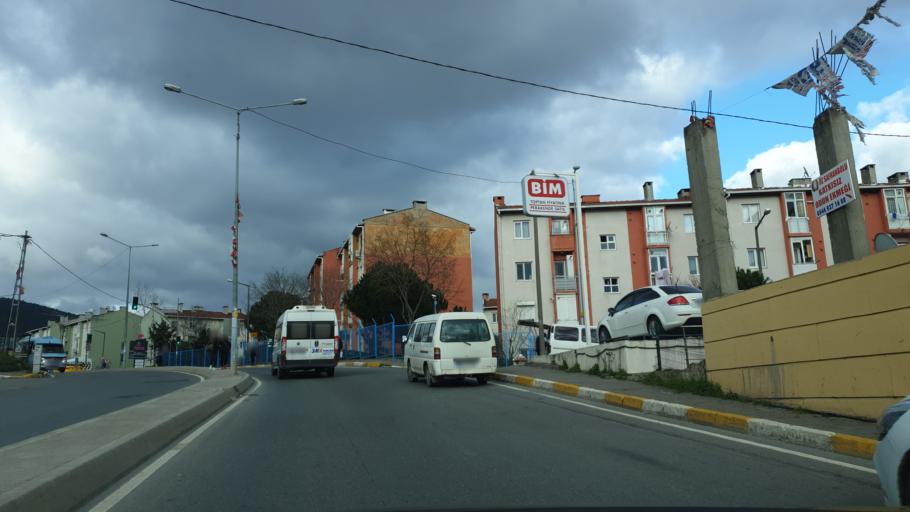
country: TR
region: Istanbul
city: Pendik
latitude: 40.9139
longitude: 29.2536
